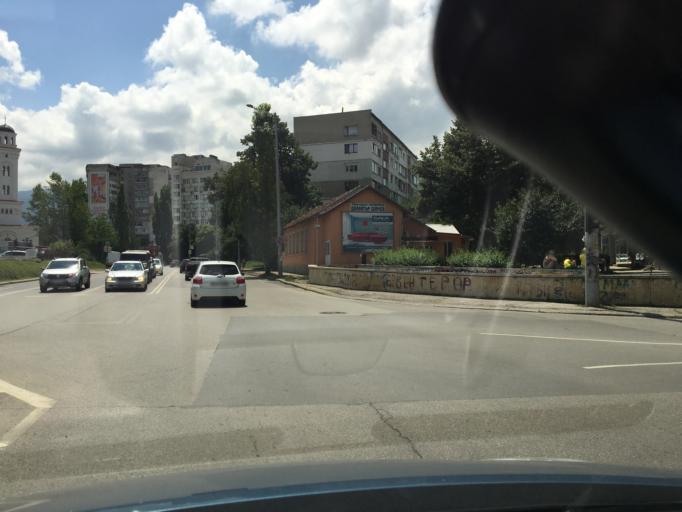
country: BG
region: Sofia-Capital
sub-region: Stolichna Obshtina
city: Sofia
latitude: 42.6654
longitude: 23.3028
